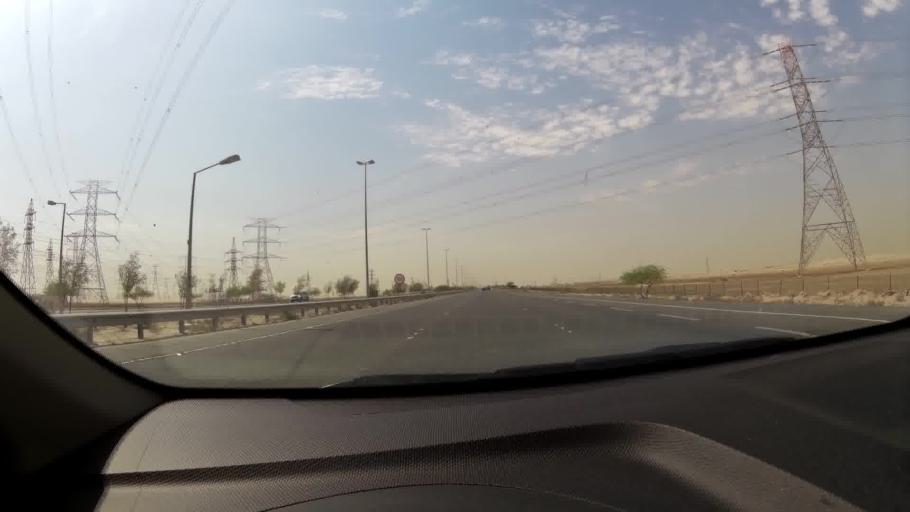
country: KW
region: Al Ahmadi
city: Al Fahahil
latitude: 28.7551
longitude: 48.2808
